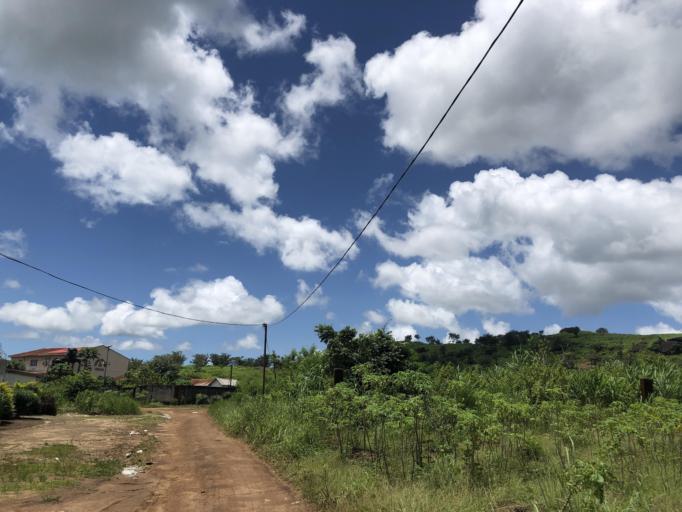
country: SL
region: Northern Province
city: Makeni
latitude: 8.8489
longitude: -12.0587
